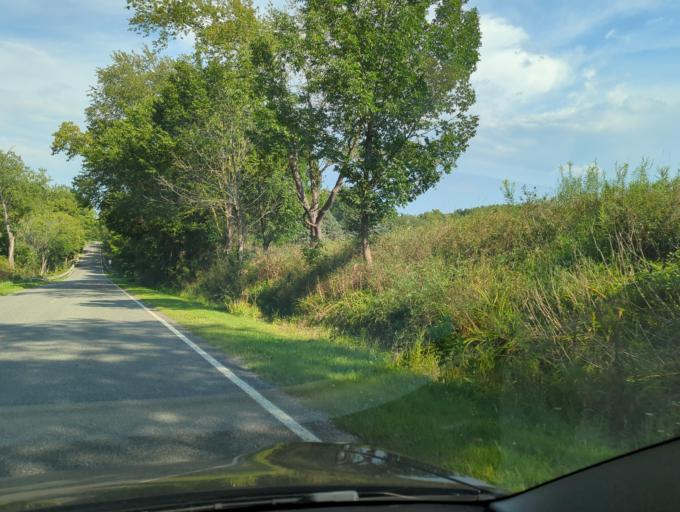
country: US
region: Michigan
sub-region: Ionia County
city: Ionia
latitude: 42.9297
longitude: -85.1237
